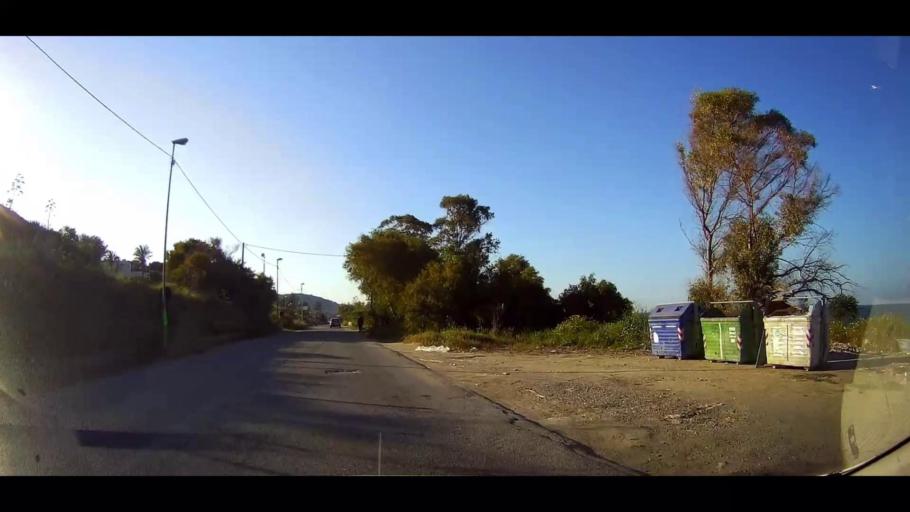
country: IT
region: Calabria
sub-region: Provincia di Crotone
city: Crotone
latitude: 39.0518
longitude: 17.1400
